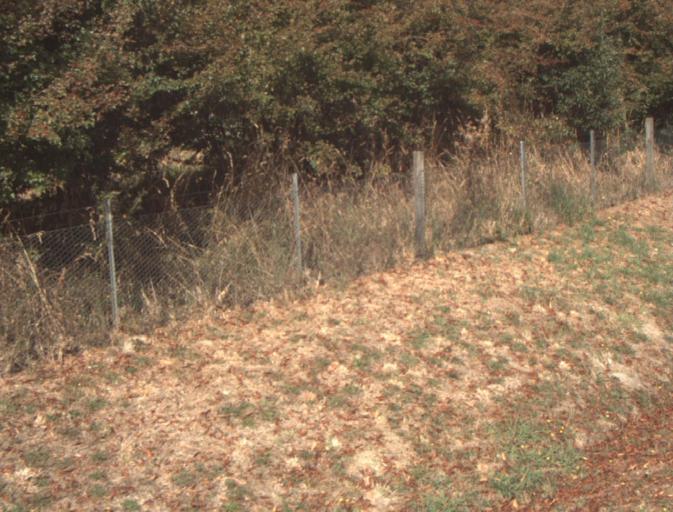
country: AU
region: Tasmania
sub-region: Launceston
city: Mayfield
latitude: -41.2574
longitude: 147.1967
